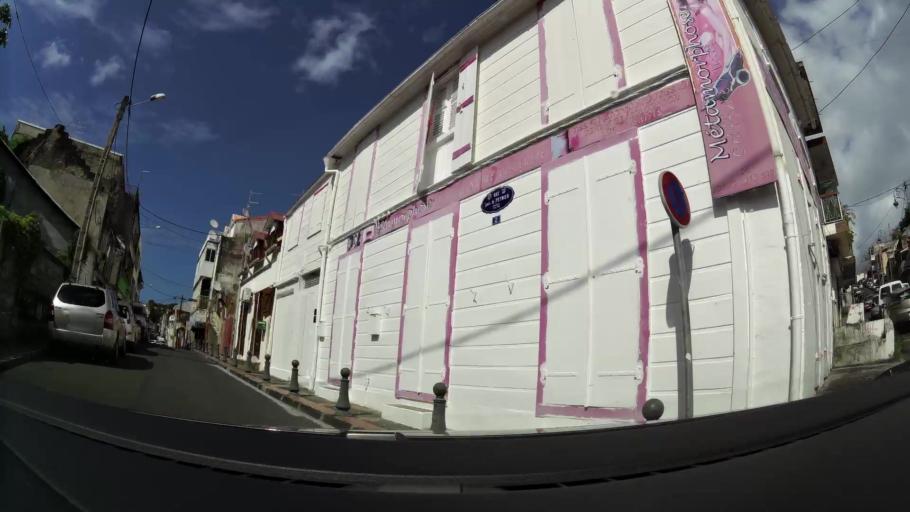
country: GP
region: Guadeloupe
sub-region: Guadeloupe
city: Basse-Terre
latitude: 15.9968
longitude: -61.7302
